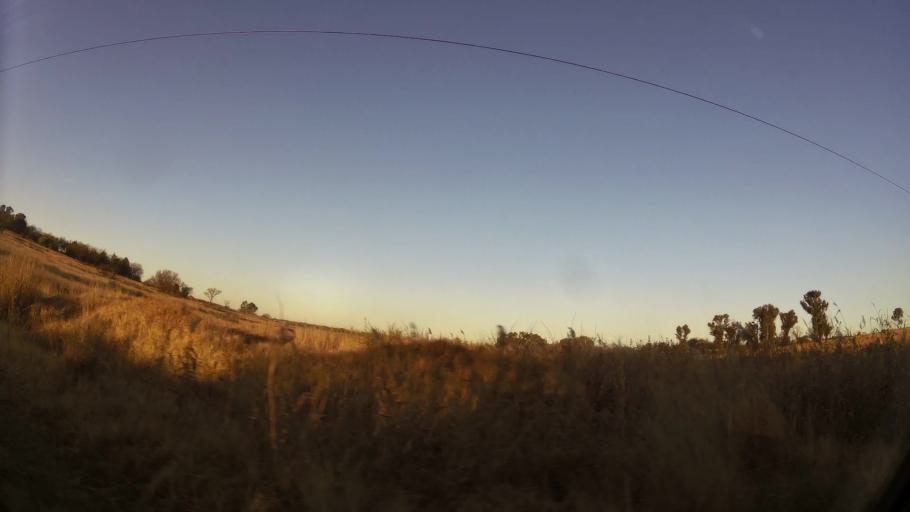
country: ZA
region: Gauteng
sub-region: City of Johannesburg Metropolitan Municipality
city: Diepsloot
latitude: -25.9550
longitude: 28.0575
